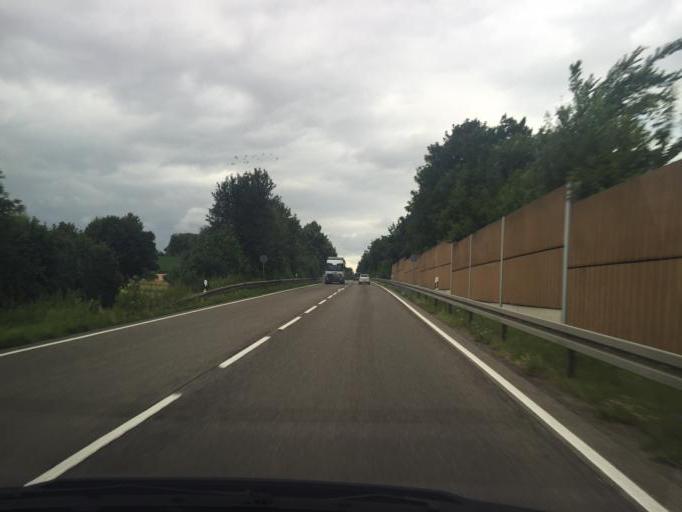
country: DE
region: Baden-Wuerttemberg
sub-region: Karlsruhe Region
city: Gondelsheim
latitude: 49.0532
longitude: 8.6596
